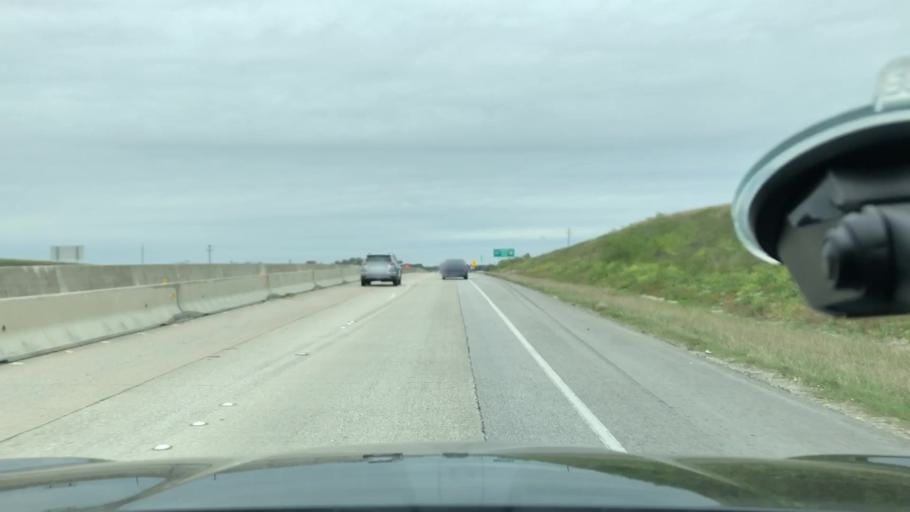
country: US
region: Texas
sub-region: Ellis County
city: Waxahachie
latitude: 32.3833
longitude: -96.8668
